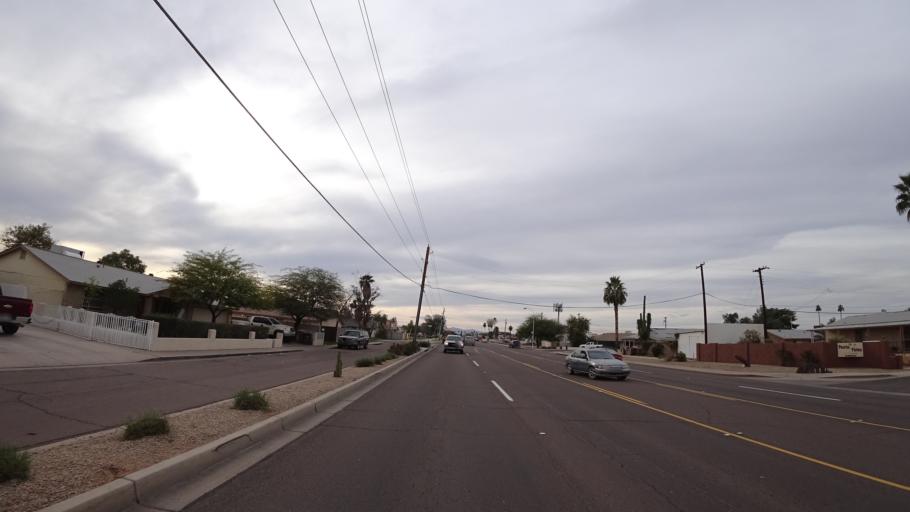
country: US
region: Arizona
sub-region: Maricopa County
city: Peoria
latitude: 33.5814
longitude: -112.2168
